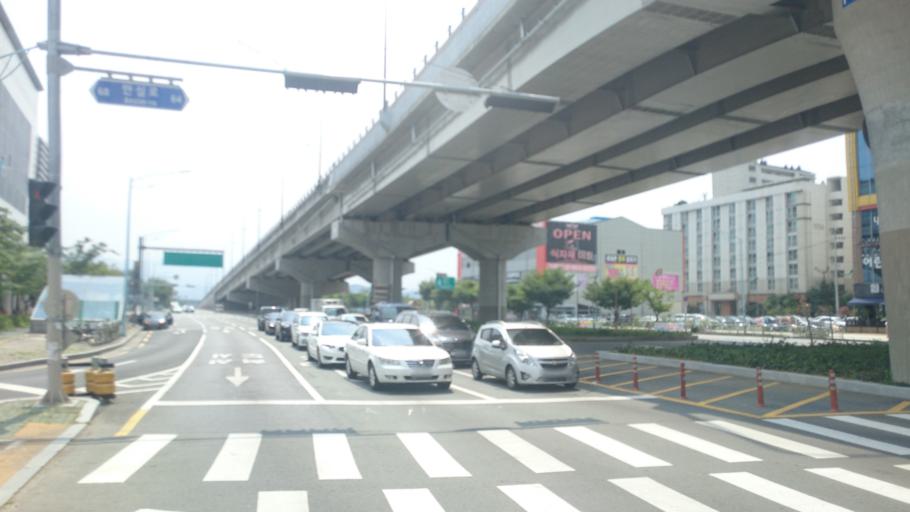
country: KR
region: Gyeongsangbuk-do
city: Gyeongsan-si
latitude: 35.8697
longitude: 128.6926
